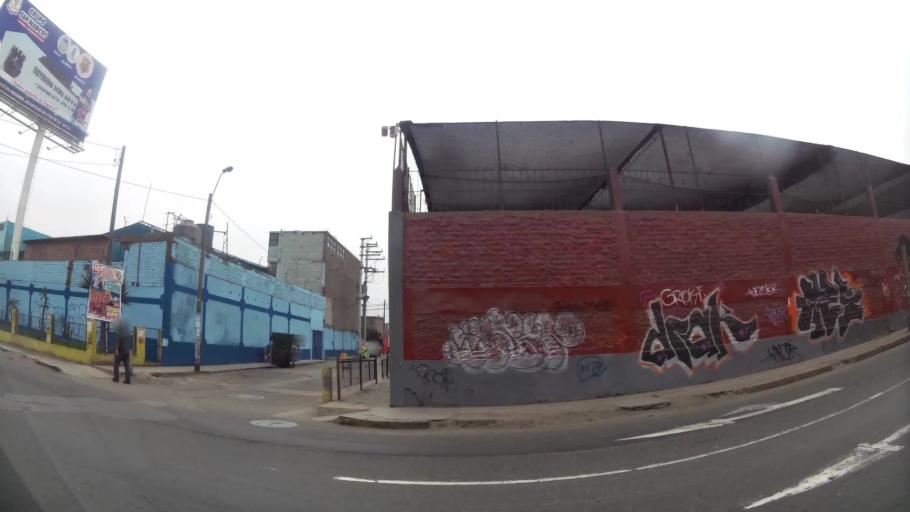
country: PE
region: Lima
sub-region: Lima
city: Vitarte
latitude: -12.0251
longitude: -76.9175
